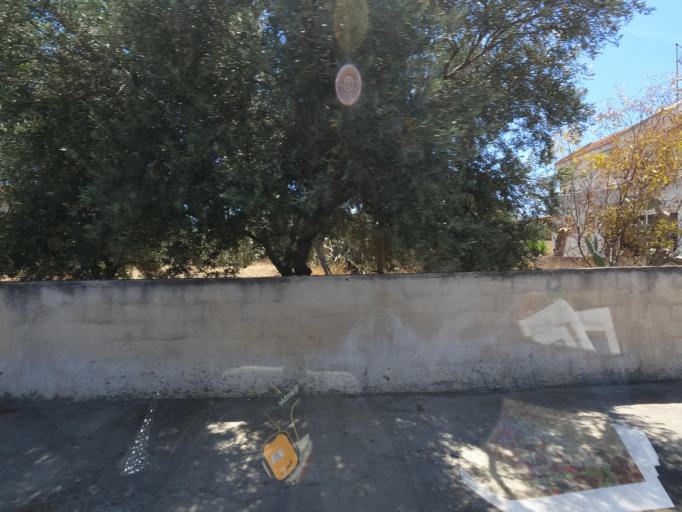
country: CY
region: Larnaka
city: Pyla
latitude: 35.0073
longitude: 33.6903
